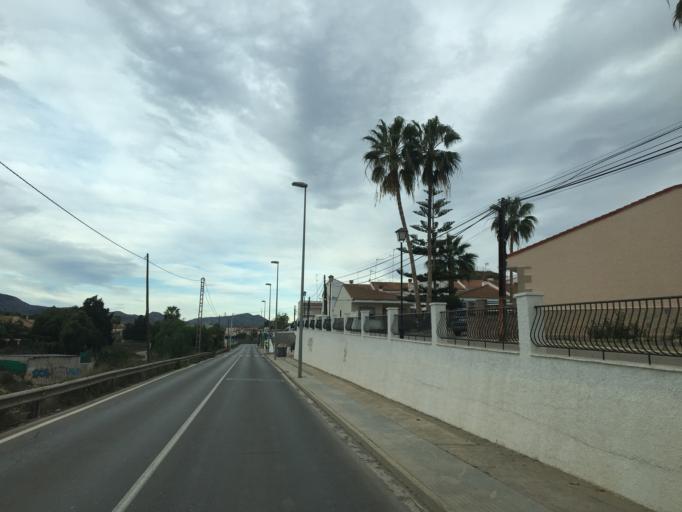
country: ES
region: Murcia
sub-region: Murcia
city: Cartagena
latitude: 37.6114
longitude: -1.0332
